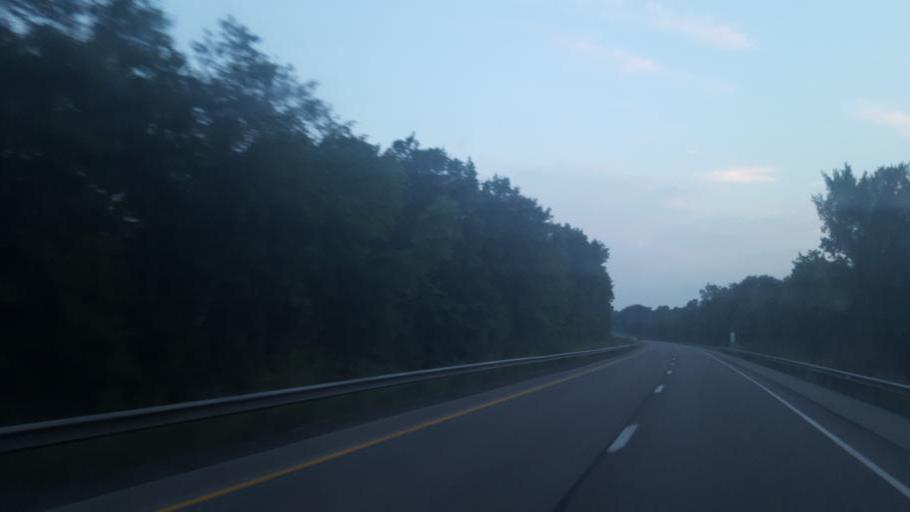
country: US
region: Pennsylvania
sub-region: Mercer County
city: Stoneboro
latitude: 41.4030
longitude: -80.1560
